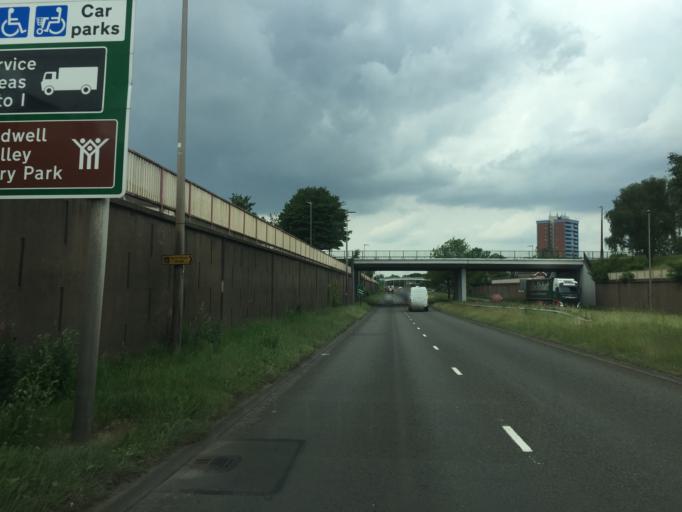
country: GB
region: England
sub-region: Sandwell
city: West Bromwich
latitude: 52.5193
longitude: -1.9860
